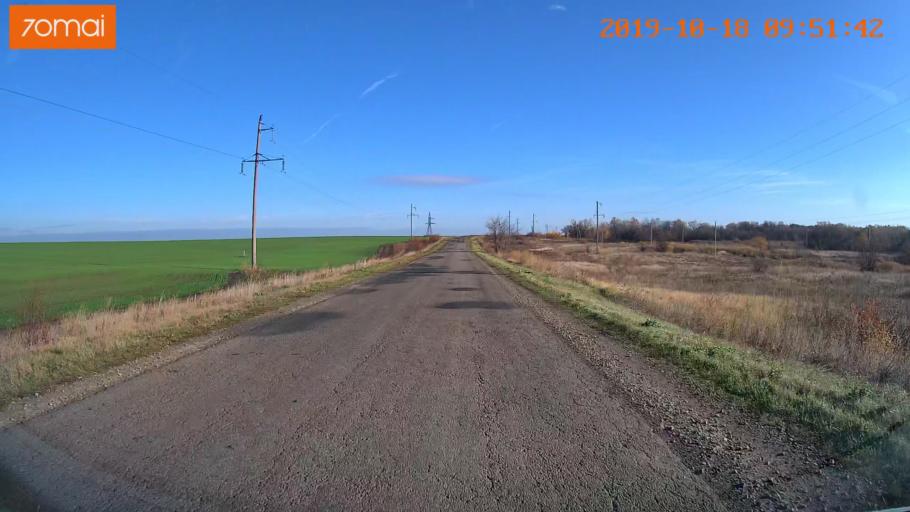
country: RU
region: Tula
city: Kazachka
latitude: 53.3440
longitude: 38.2968
